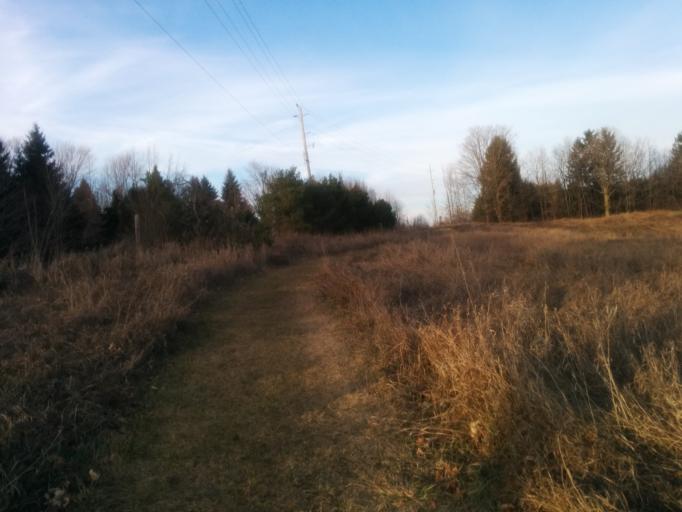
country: CA
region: Ontario
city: Orangeville
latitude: 43.9614
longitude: -79.9796
